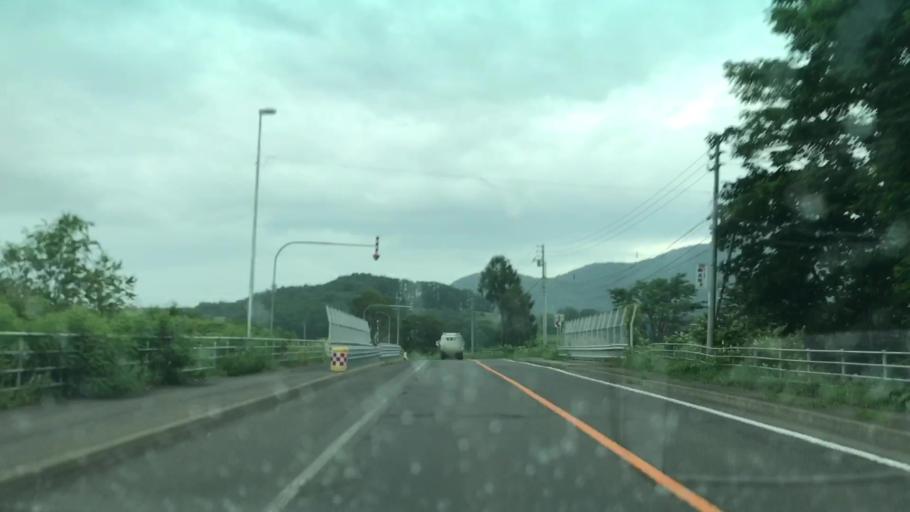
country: JP
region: Hokkaido
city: Niseko Town
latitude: 42.8100
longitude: 140.5376
